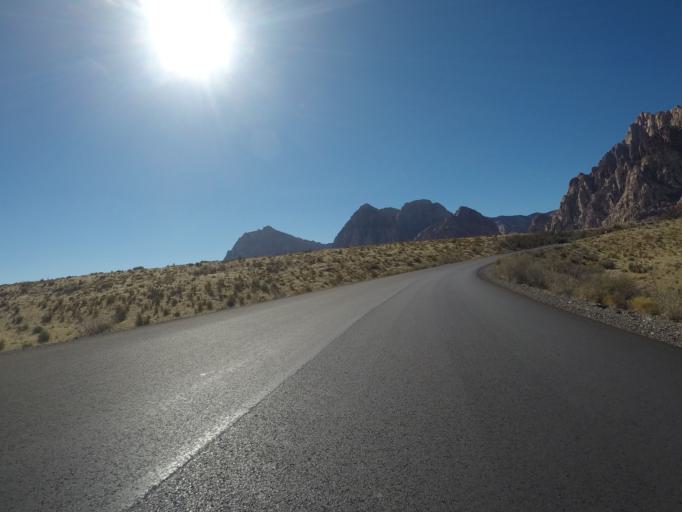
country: US
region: Nevada
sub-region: Clark County
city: Summerlin South
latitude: 36.1387
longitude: -115.4667
